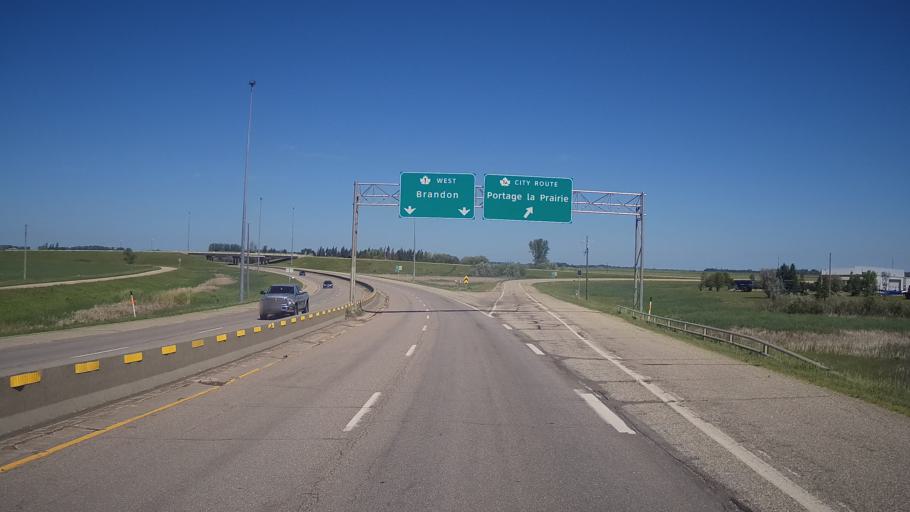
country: CA
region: Manitoba
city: Portage la Prairie
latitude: 49.9703
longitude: -98.3587
